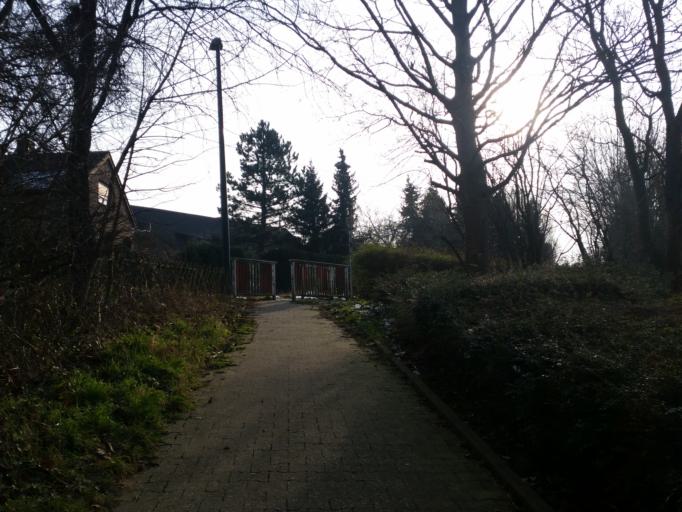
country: DE
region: North Rhine-Westphalia
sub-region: Regierungsbezirk Koln
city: Wurselen
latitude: 50.7907
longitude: 6.1237
